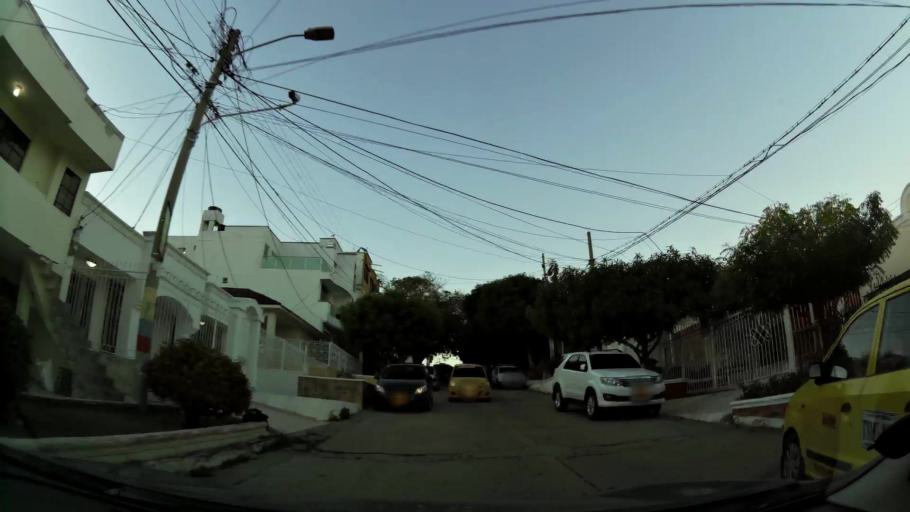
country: CO
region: Atlantico
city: Barranquilla
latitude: 10.9823
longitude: -74.8073
